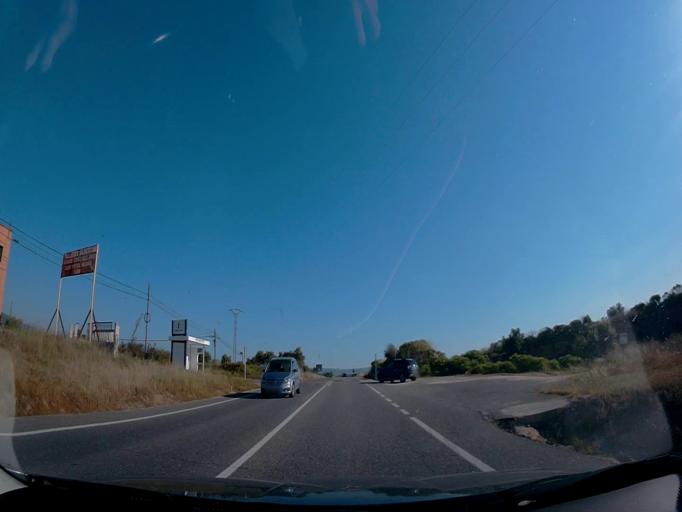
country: ES
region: Castille-La Mancha
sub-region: Province of Toledo
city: Escalona
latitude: 40.1441
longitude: -4.4033
